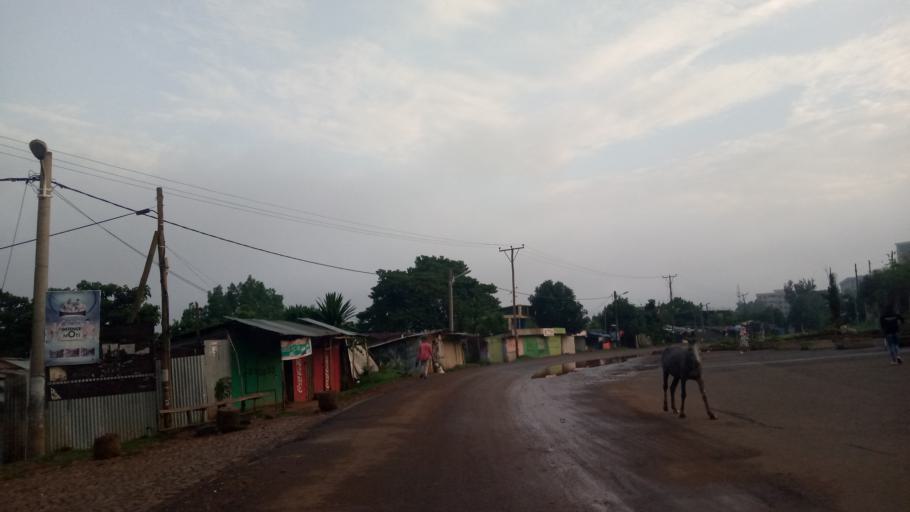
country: ET
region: Oromiya
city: Jima
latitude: 7.6784
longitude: 36.8507
